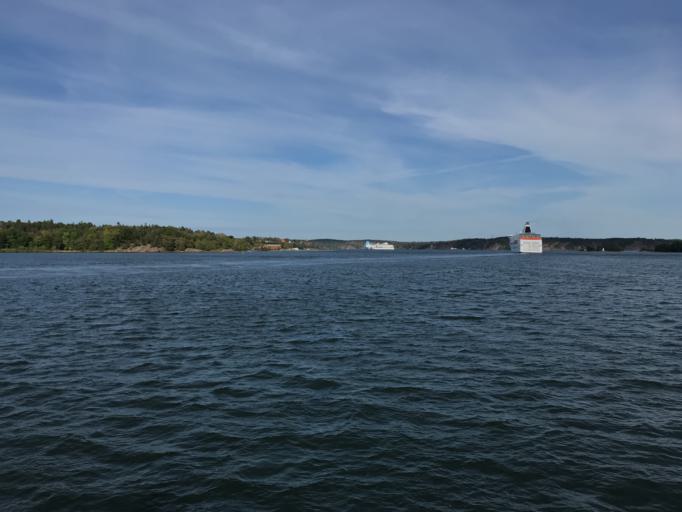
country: SE
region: Stockholm
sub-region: Nacka Kommun
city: Nacka
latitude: 59.3377
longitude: 18.1530
